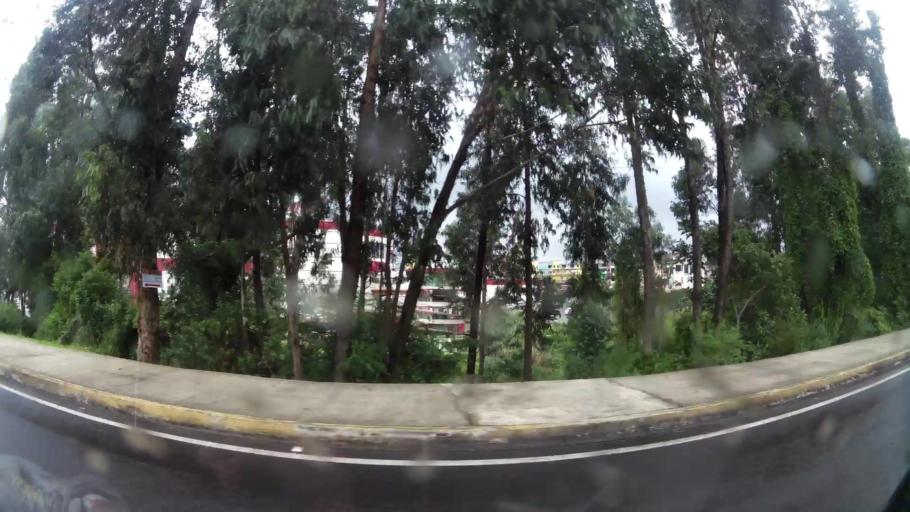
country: EC
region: Pichincha
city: Sangolqui
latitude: -0.3231
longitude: -78.4483
